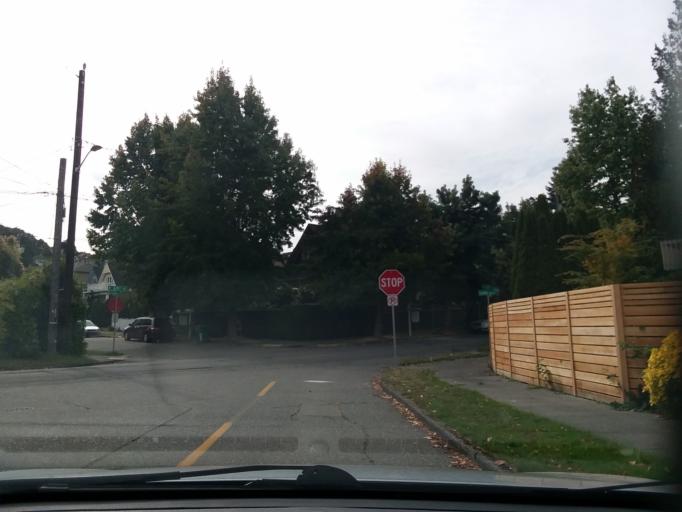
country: US
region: Washington
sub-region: King County
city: Seattle
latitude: 47.6762
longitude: -122.3482
